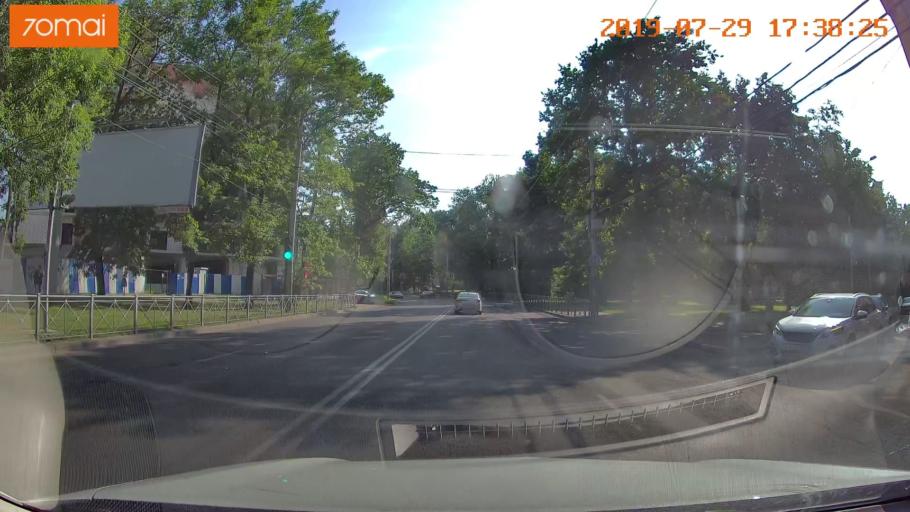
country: RU
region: Kaliningrad
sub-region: Gorod Kaliningrad
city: Kaliningrad
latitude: 54.7232
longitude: 20.5081
